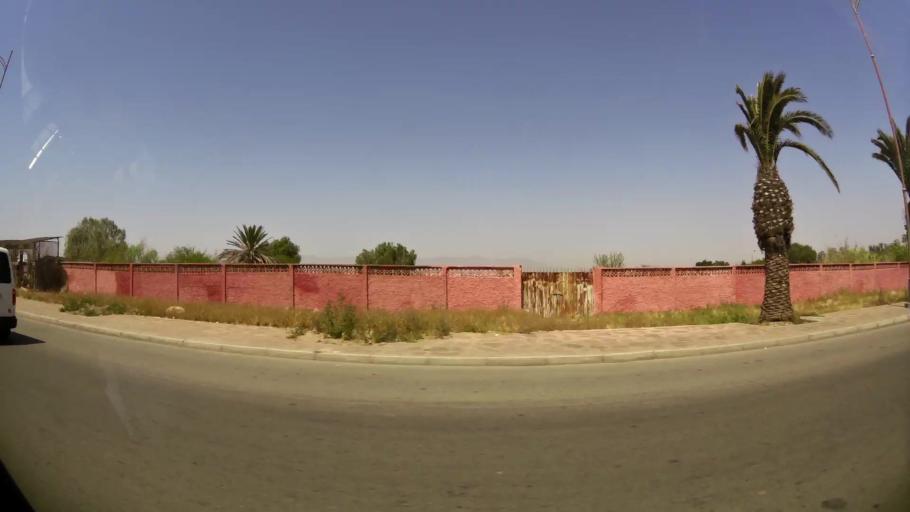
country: MA
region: Souss-Massa-Draa
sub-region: Inezgane-Ait Mellou
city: Inezgane
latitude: 30.3580
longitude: -9.5201
